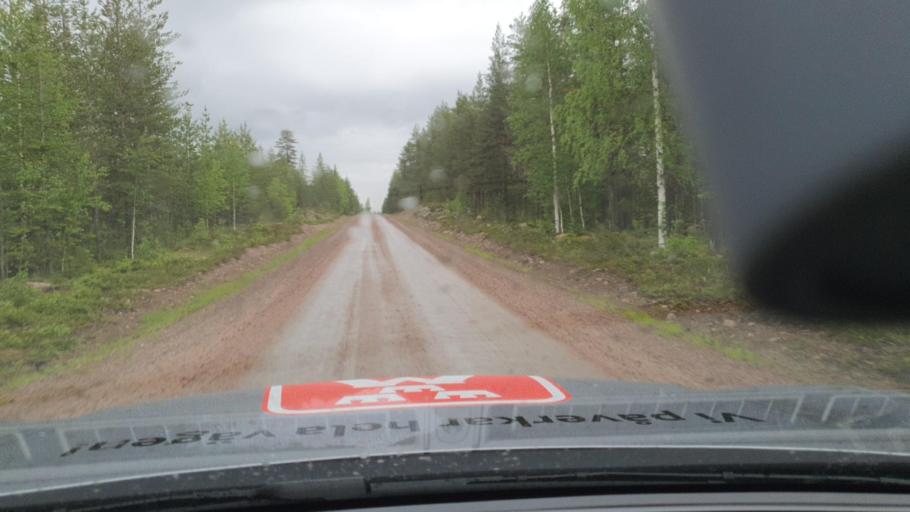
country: SE
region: Norrbotten
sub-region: Overkalix Kommun
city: OEverkalix
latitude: 66.6436
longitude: 22.6999
